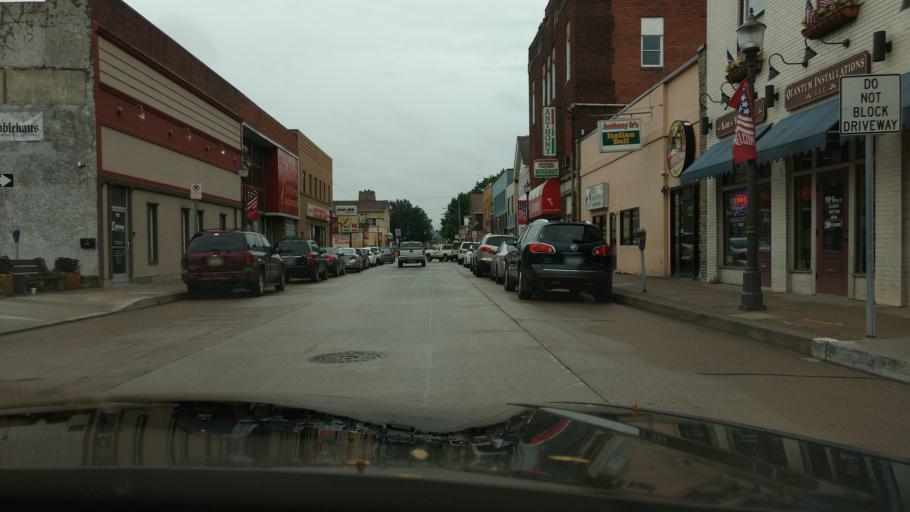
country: US
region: Pennsylvania
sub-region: Allegheny County
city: Coraopolis
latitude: 40.5173
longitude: -80.1638
